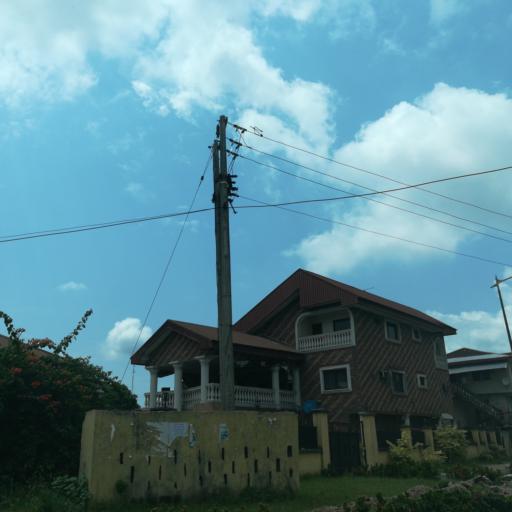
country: NG
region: Rivers
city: Port Harcourt
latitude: 4.8082
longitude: 7.0024
